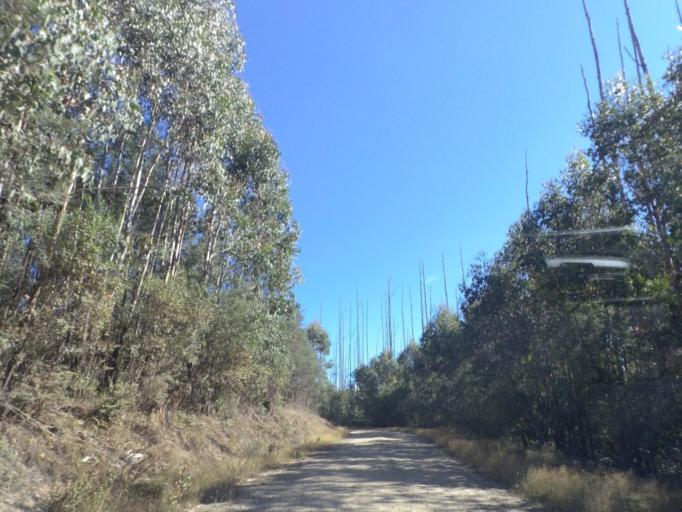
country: AU
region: Victoria
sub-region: Murrindindi
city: Alexandra
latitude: -37.4158
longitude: 145.8003
